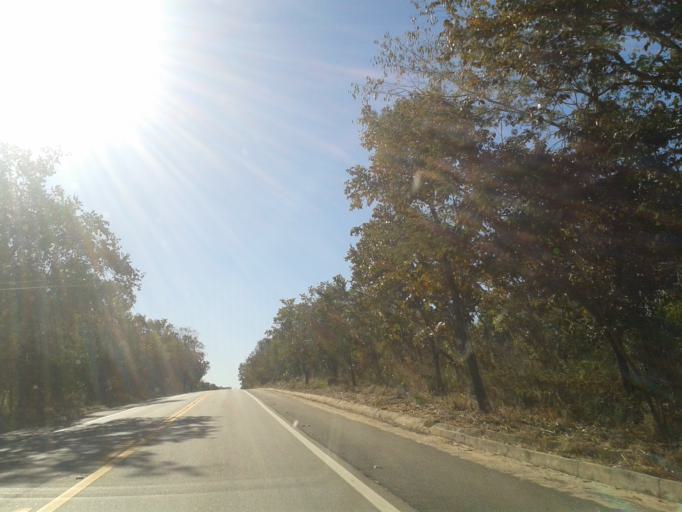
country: BR
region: Goias
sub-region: Itapuranga
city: Itapuranga
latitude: -15.3394
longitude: -50.4139
